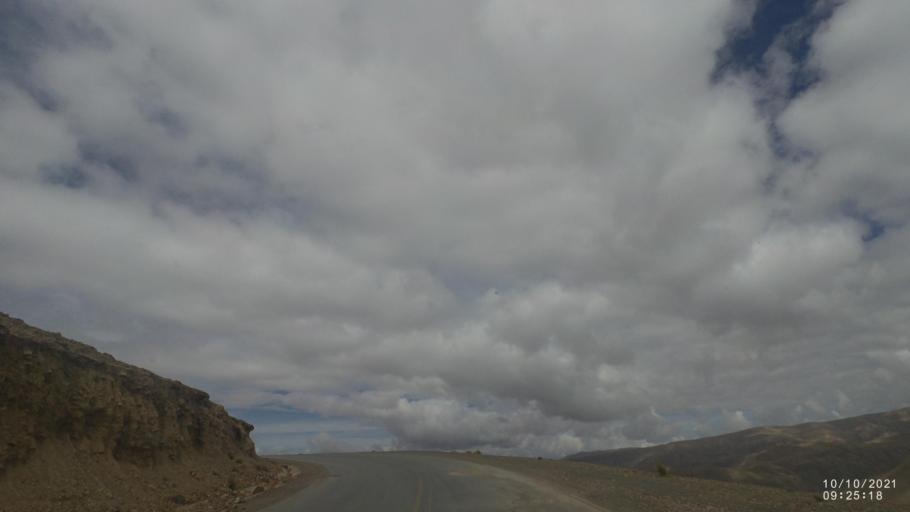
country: BO
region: La Paz
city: Quime
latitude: -17.0903
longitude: -67.3154
